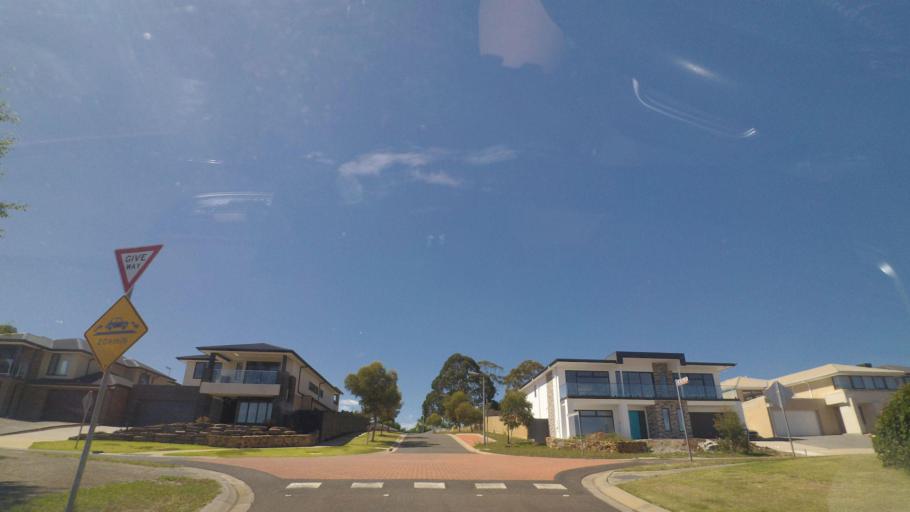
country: AU
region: Victoria
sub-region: Yarra Ranges
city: Lilydale
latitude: -37.7625
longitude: 145.3285
